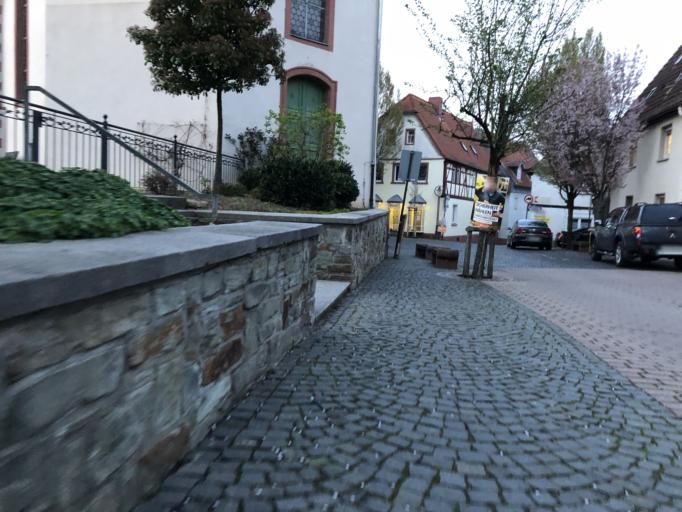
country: DE
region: Hesse
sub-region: Regierungsbezirk Darmstadt
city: Hochheim am Main
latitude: 50.0617
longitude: 8.3721
